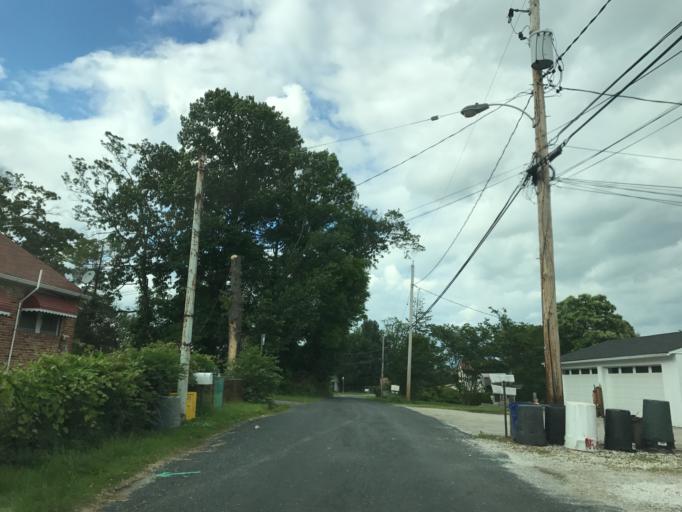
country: US
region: Maryland
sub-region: Baltimore County
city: Edgemere
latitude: 39.2835
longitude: -76.4107
